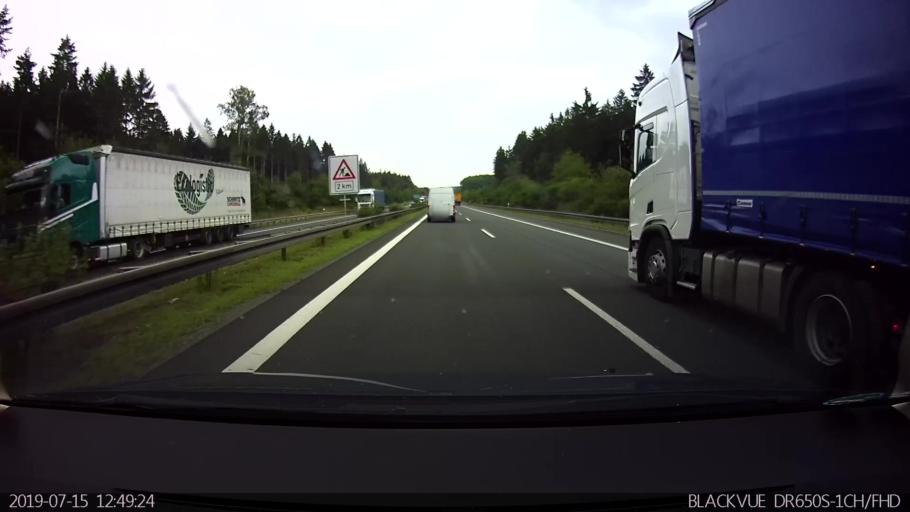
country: DE
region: Saxony
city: Waldkirchen
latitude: 50.6188
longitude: 12.4127
